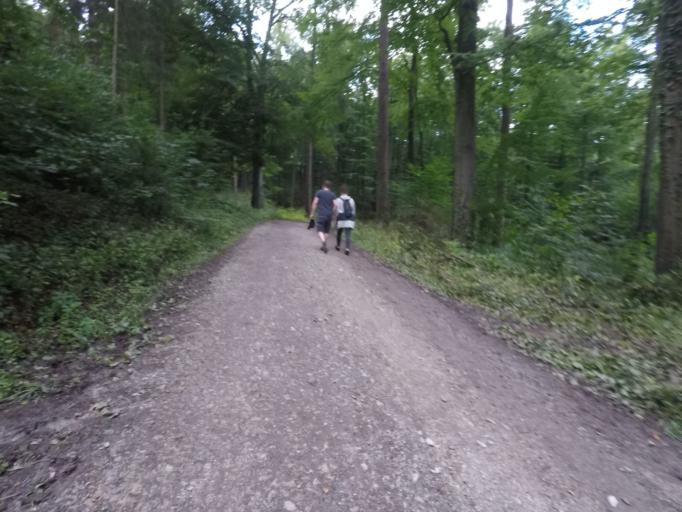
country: DE
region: North Rhine-Westphalia
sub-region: Regierungsbezirk Detmold
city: Bielefeld
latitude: 52.0311
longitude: 8.4941
